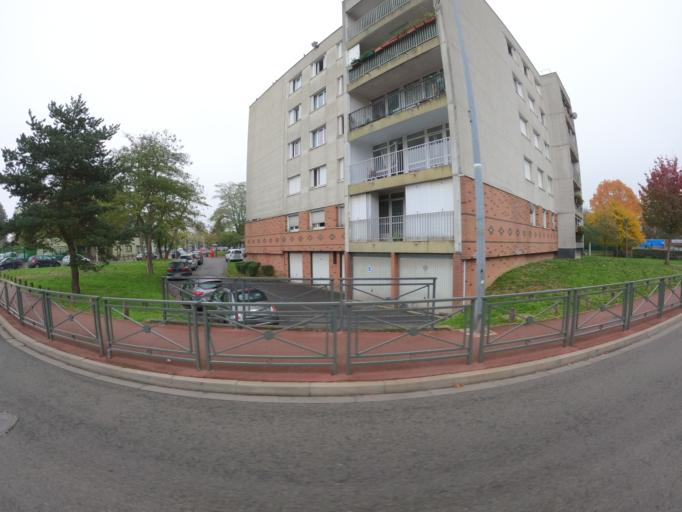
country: FR
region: Ile-de-France
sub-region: Departement du Val-de-Marne
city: Chennevieres-sur-Marne
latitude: 48.8024
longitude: 2.5527
